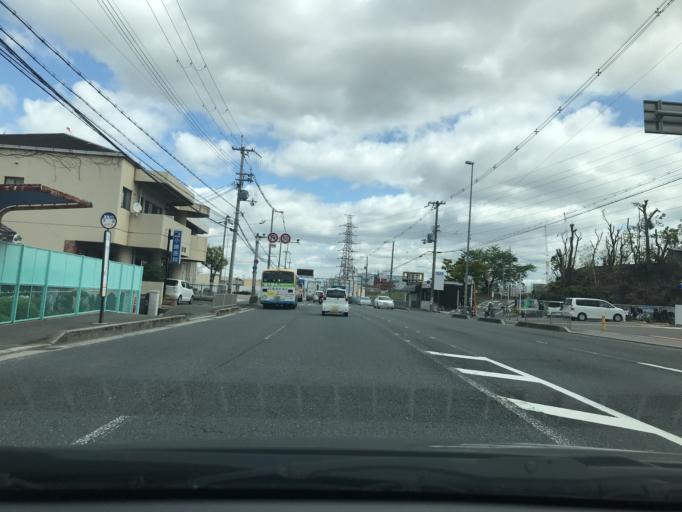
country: JP
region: Osaka
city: Ibaraki
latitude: 34.8363
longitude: 135.5493
